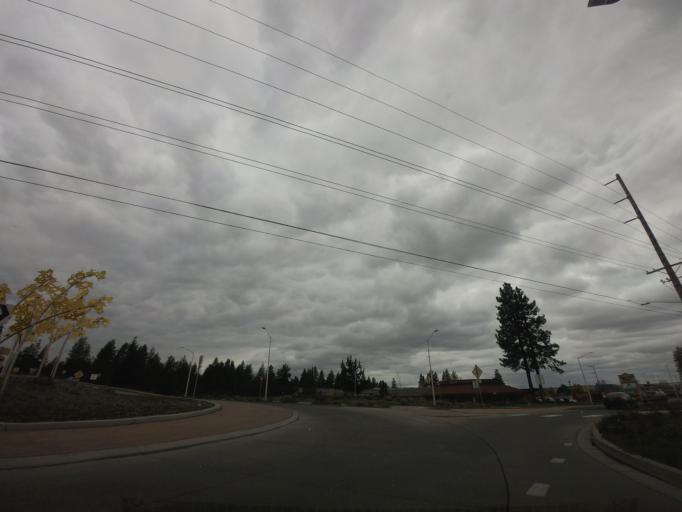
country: US
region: Oregon
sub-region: Deschutes County
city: Bend
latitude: 44.0194
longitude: -121.3170
